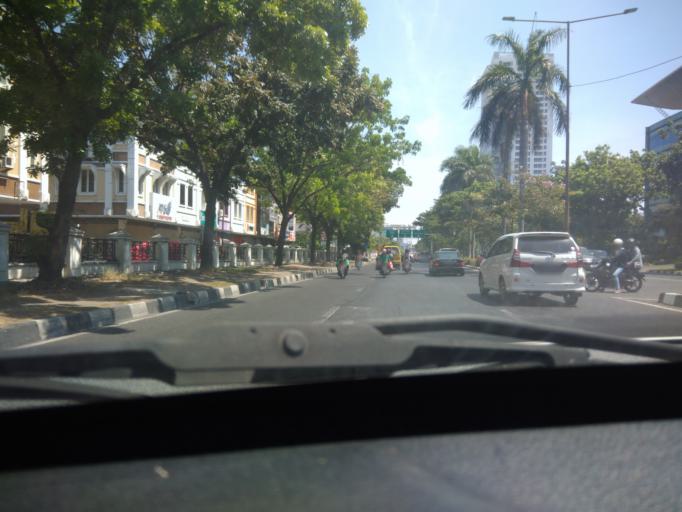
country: ID
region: East Java
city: Mulyorejo
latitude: -7.2832
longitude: 112.7808
